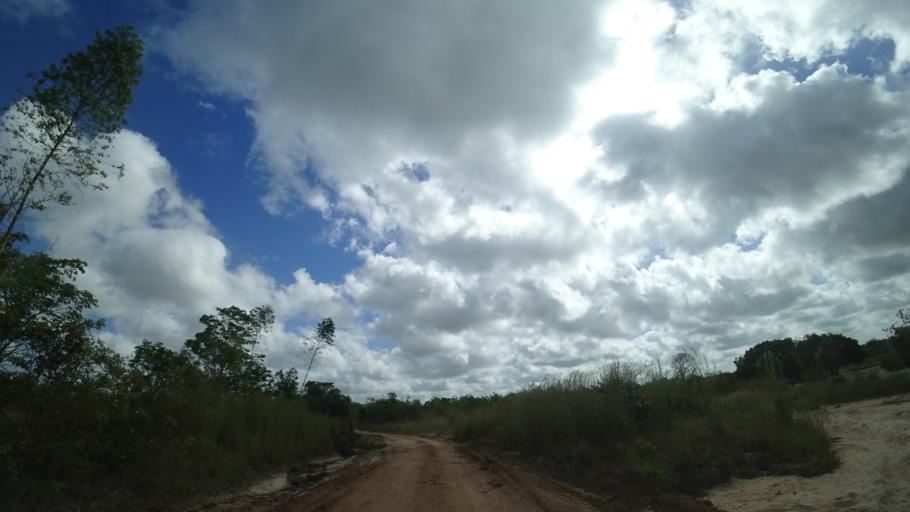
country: MZ
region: Sofala
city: Dondo
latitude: -19.4373
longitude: 34.7138
